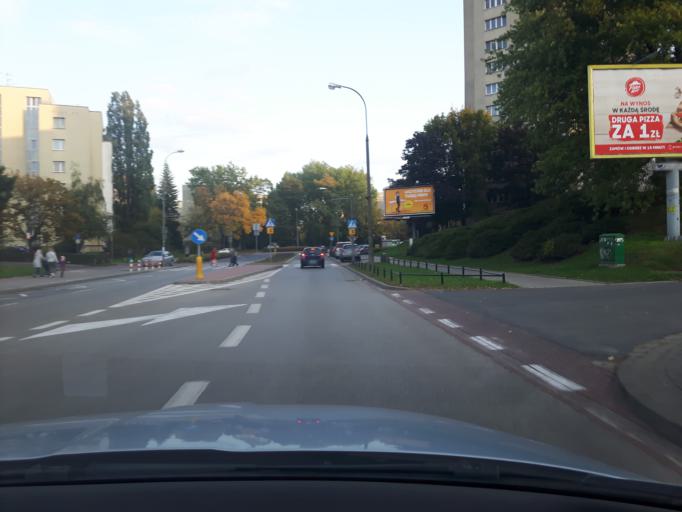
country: PL
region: Masovian Voivodeship
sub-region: Warszawa
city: Ursynow
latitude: 52.1546
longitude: 21.0297
